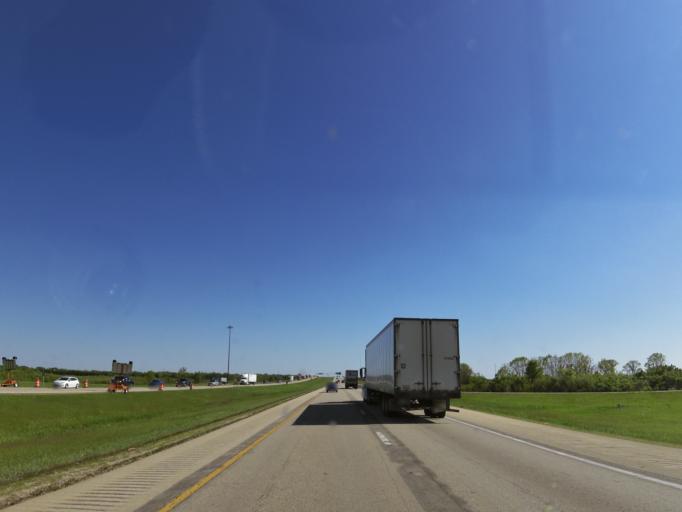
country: US
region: Illinois
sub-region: Ogle County
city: Hillcrest
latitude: 41.9329
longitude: -89.0244
